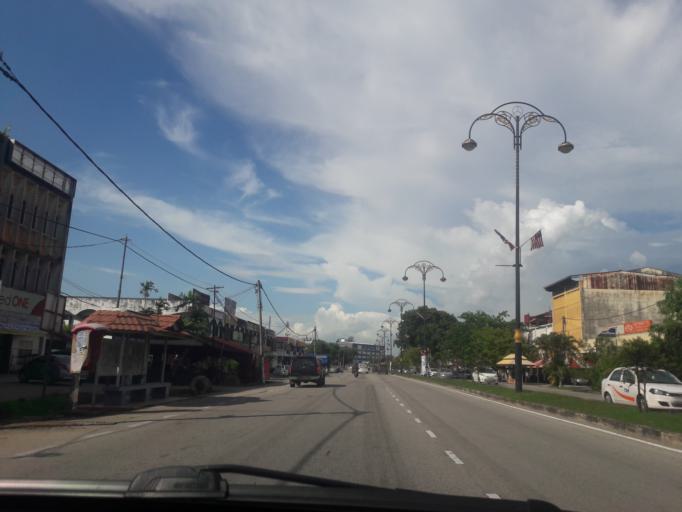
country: MY
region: Kedah
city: Sungai Petani
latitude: 5.6321
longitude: 100.4823
